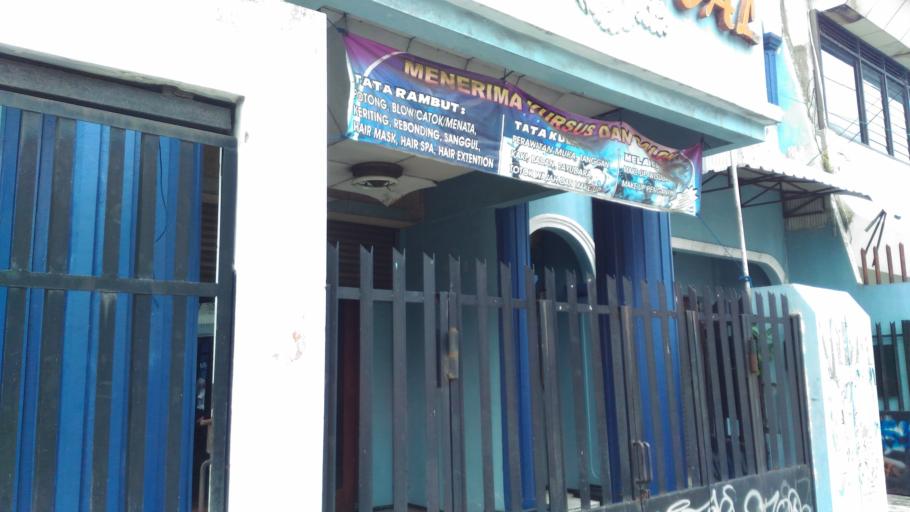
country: ID
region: Daerah Istimewa Yogyakarta
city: Yogyakarta
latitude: -7.8023
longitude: 110.3787
